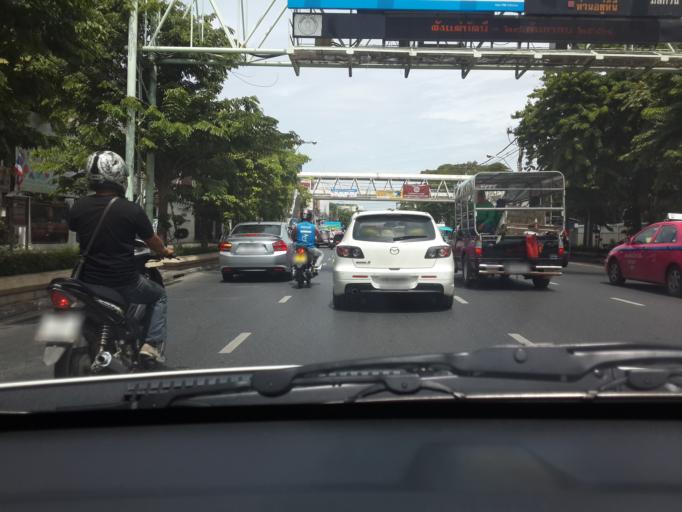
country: TH
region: Bangkok
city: Pom Prap Sattru Phai
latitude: 13.7569
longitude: 100.5194
